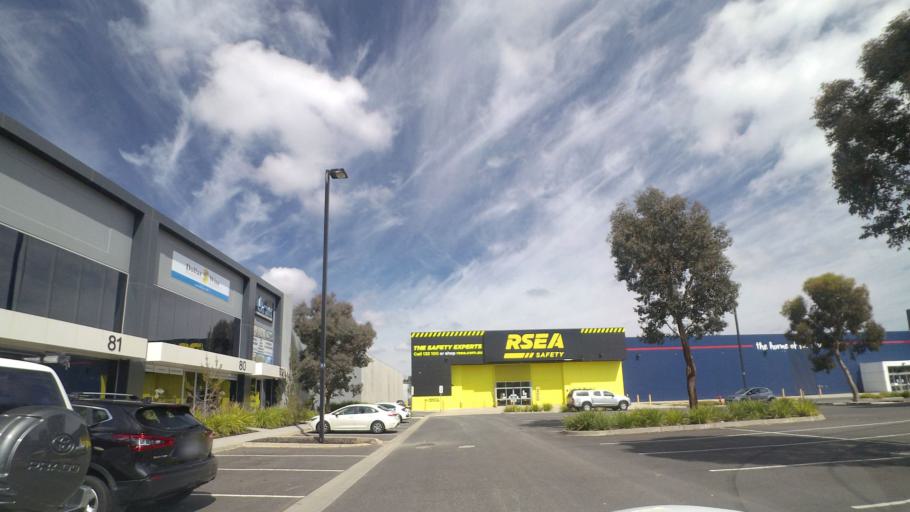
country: AU
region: Victoria
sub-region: Knox
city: Scoresby
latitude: -37.8996
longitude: 145.2422
